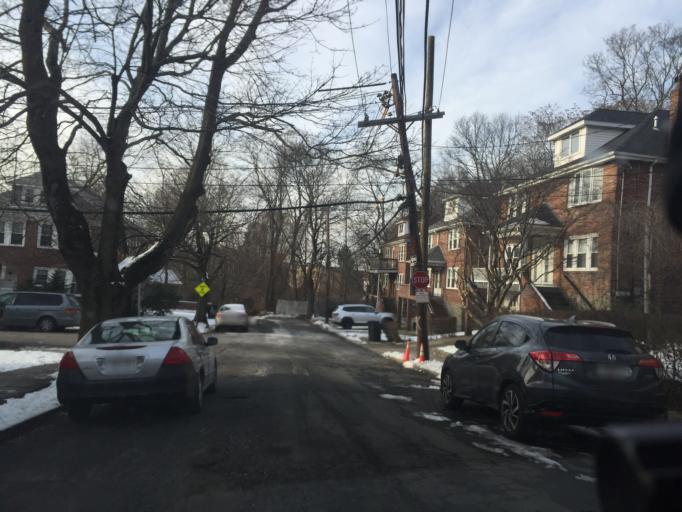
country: US
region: Massachusetts
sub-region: Norfolk County
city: Brookline
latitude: 42.3439
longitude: -71.1552
